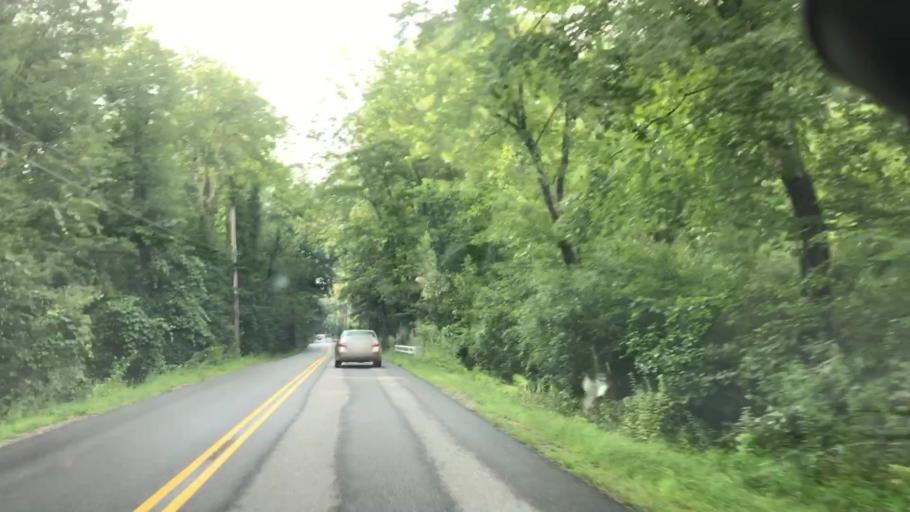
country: US
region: New Hampshire
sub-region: Hillsborough County
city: Milford
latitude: 42.8399
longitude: -71.6018
